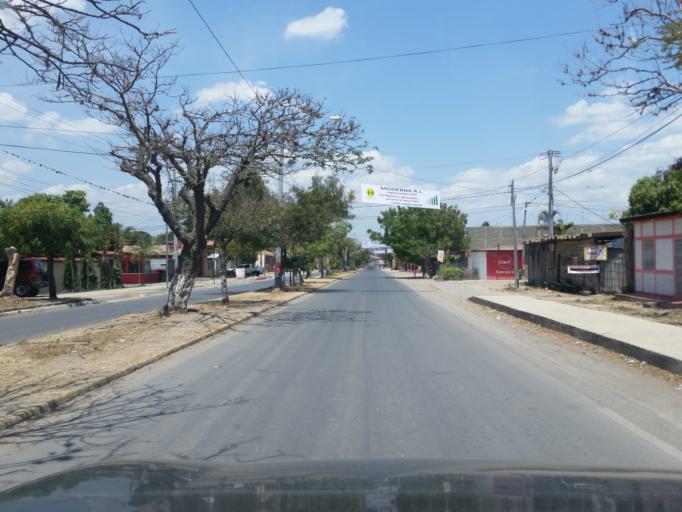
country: NI
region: Esteli
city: Esteli
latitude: 13.0754
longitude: -86.3540
